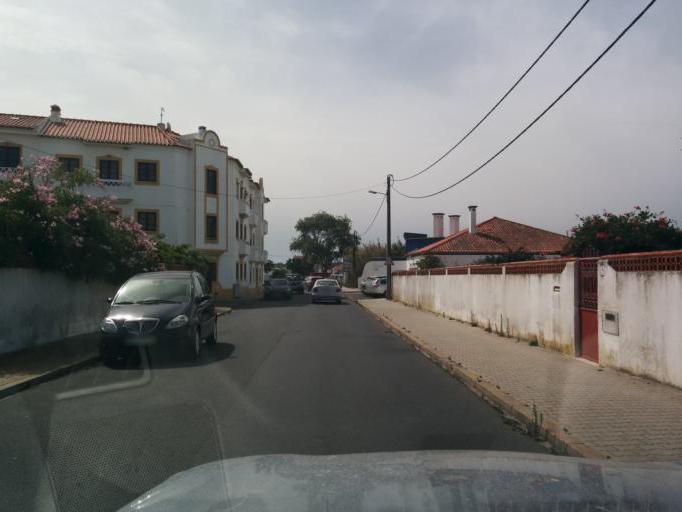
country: PT
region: Beja
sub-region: Odemira
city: Vila Nova de Milfontes
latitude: 37.7267
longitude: -8.7847
